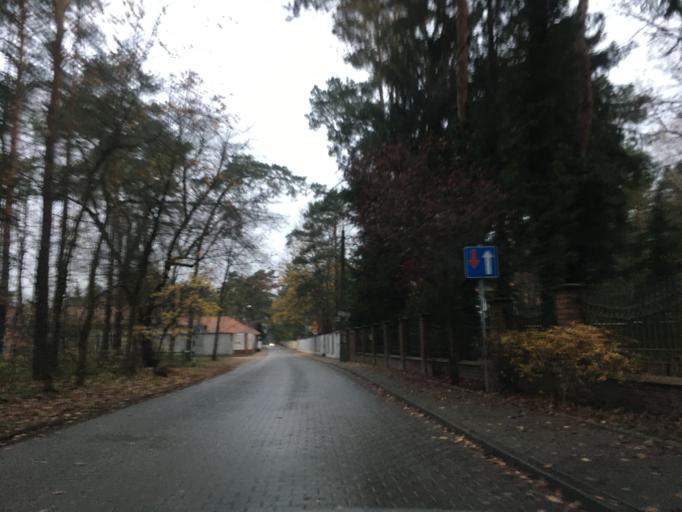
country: PL
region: Masovian Voivodeship
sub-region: Powiat piaseczynski
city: Lesznowola
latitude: 52.0900
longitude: 20.8967
